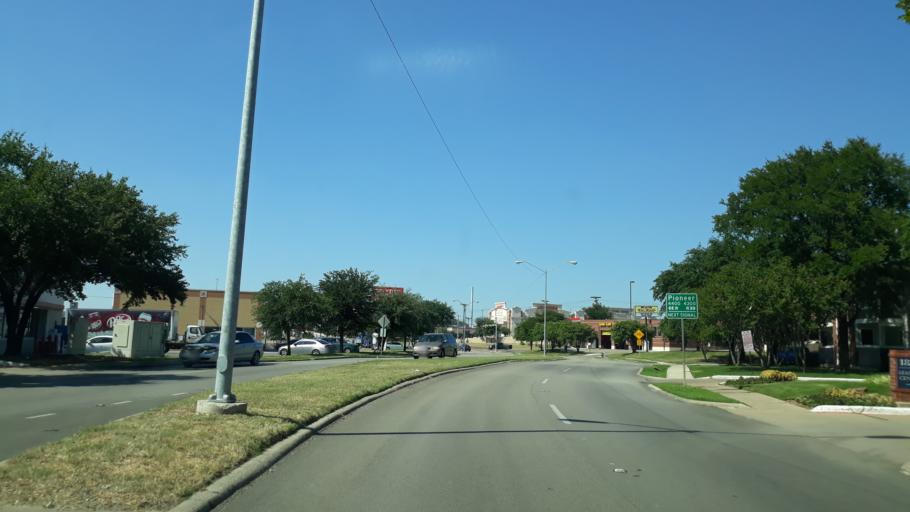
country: US
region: Texas
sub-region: Dallas County
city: Irving
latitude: 32.8316
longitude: -97.0101
